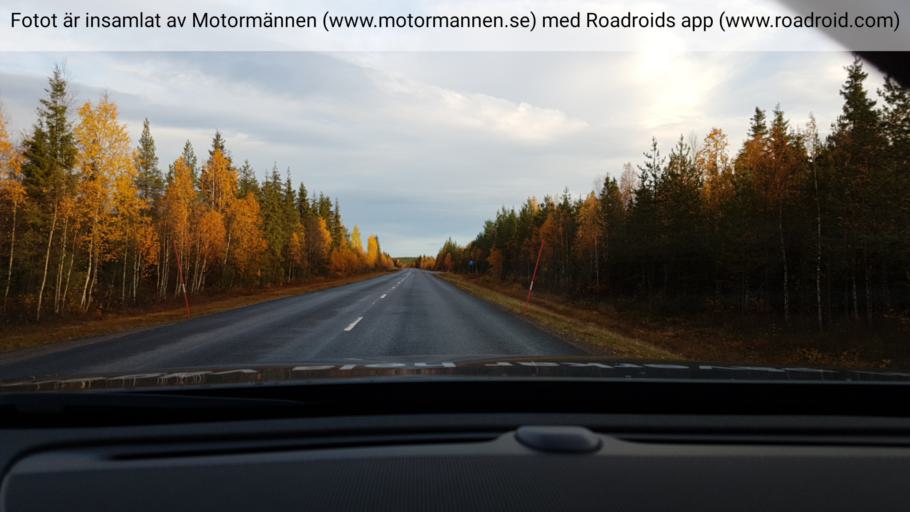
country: SE
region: Norrbotten
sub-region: Overkalix Kommun
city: OEverkalix
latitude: 66.9938
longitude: 22.5787
